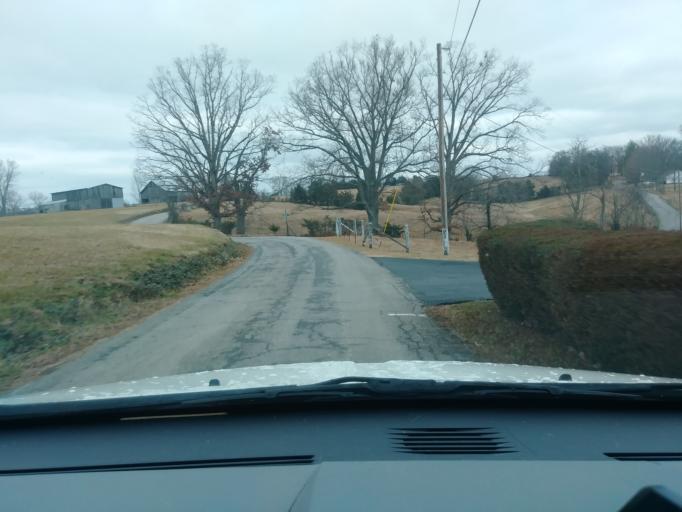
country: US
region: Tennessee
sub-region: Greene County
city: Greeneville
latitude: 36.1005
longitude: -82.8896
